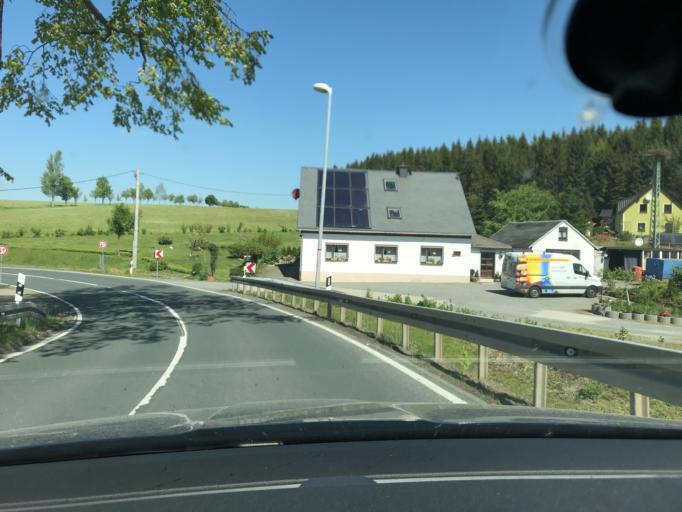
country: CZ
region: Ustecky
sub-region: Okres Chomutov
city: Vejprty
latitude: 50.4685
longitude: 12.9879
